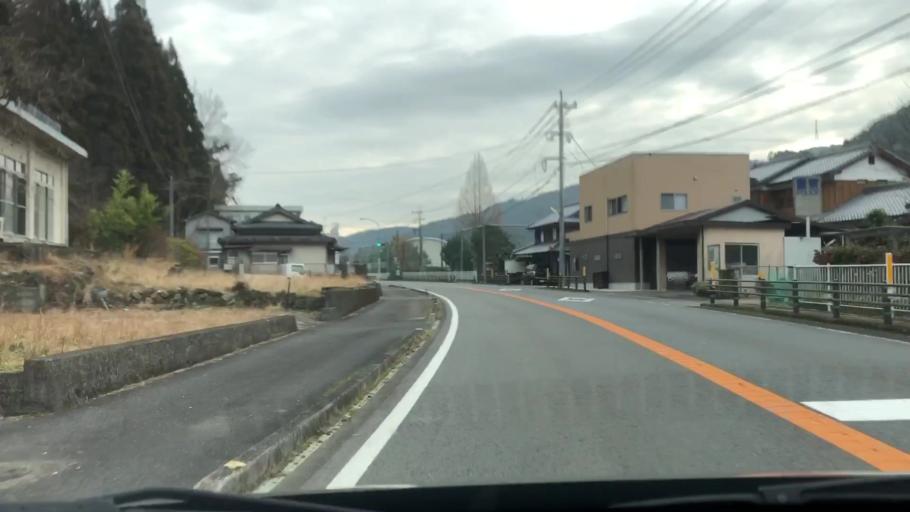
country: JP
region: Oita
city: Usuki
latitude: 33.0065
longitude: 131.7165
